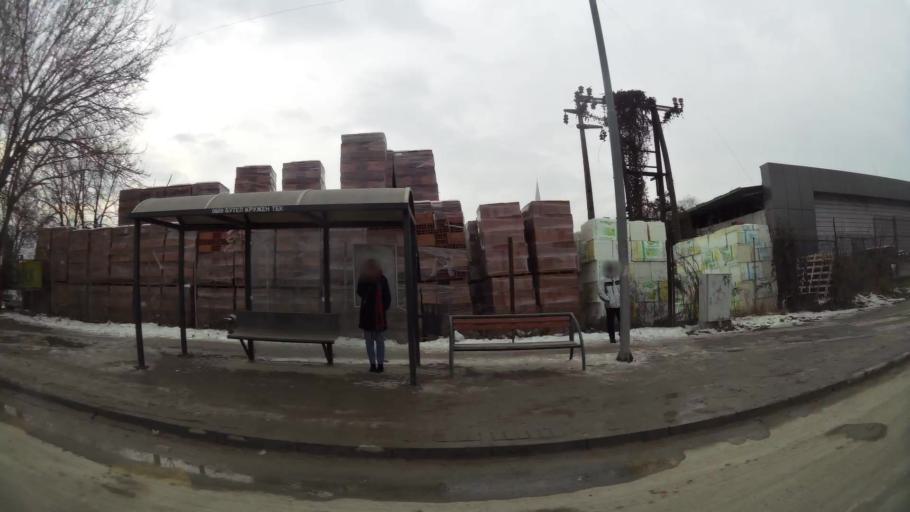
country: MK
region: Butel
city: Butel
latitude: 42.0282
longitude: 21.4446
